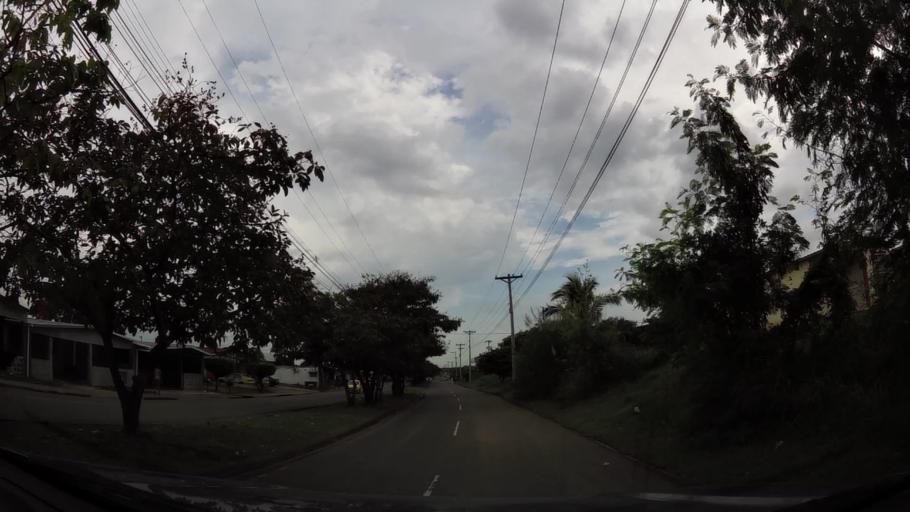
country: PA
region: Panama
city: Cabra Numero Uno
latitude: 9.0963
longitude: -79.3487
